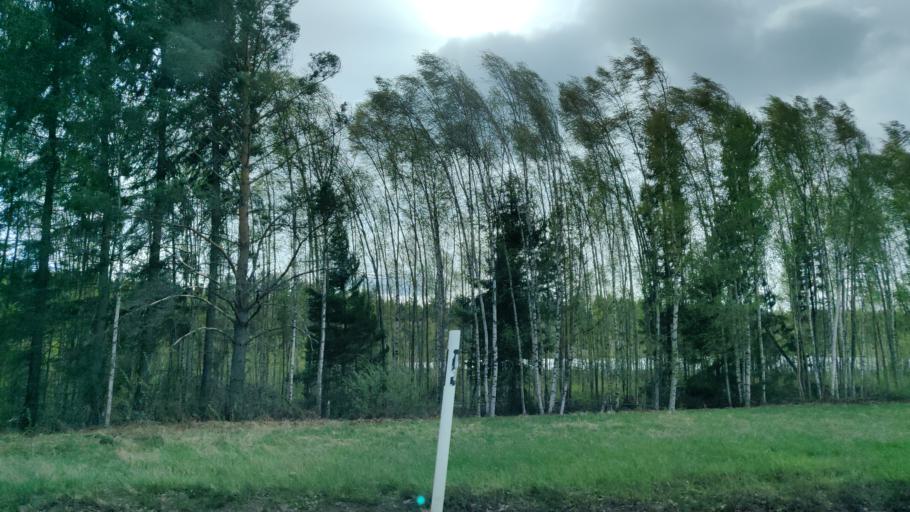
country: SE
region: Vaermland
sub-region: Forshaga Kommun
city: Deje
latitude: 59.6216
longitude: 13.4458
